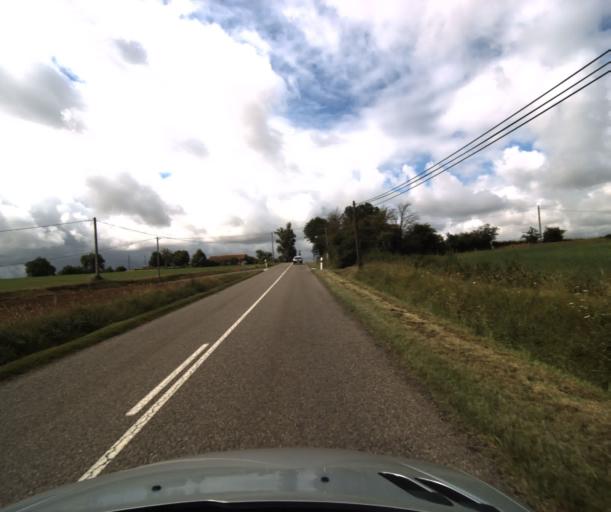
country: FR
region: Midi-Pyrenees
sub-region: Departement du Tarn-et-Garonne
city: Saint-Nicolas-de-la-Grave
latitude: 44.0011
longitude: 0.9882
